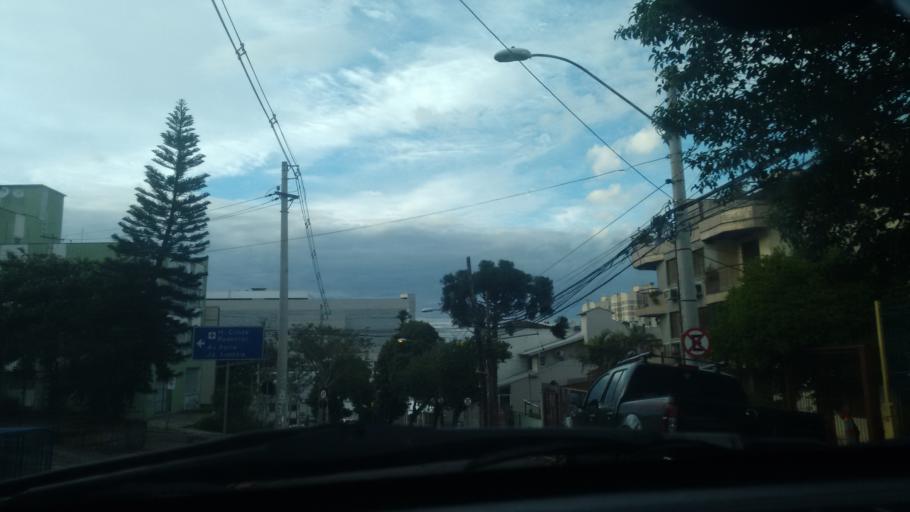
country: BR
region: Rio Grande do Sul
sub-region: Porto Alegre
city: Porto Alegre
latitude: -30.0092
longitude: -51.1617
